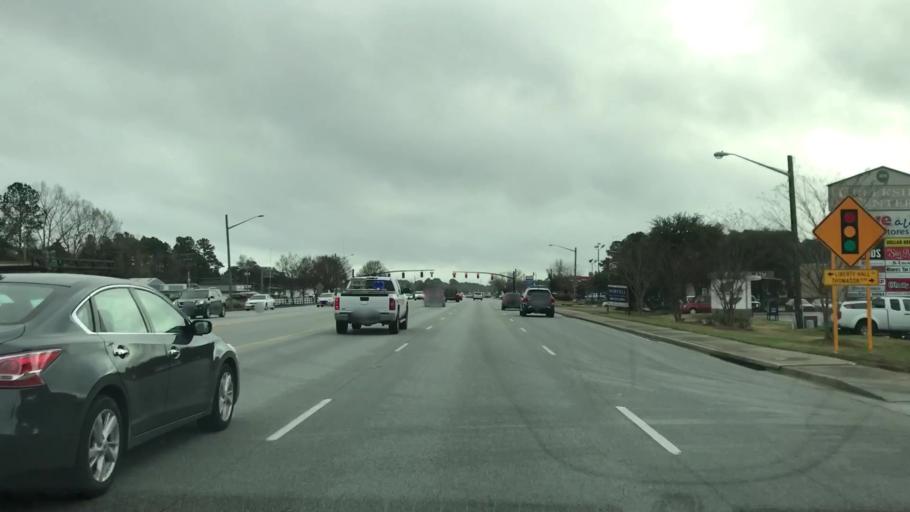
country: US
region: South Carolina
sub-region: Berkeley County
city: Goose Creek
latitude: 33.0030
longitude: -80.0380
